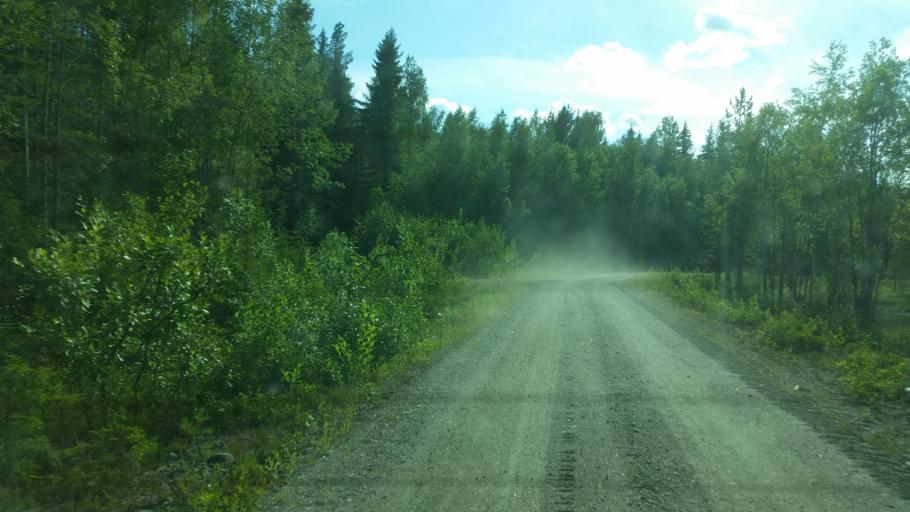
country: SE
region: Vaesternorrland
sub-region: Ange Kommun
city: Ange
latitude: 62.2717
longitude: 15.3927
